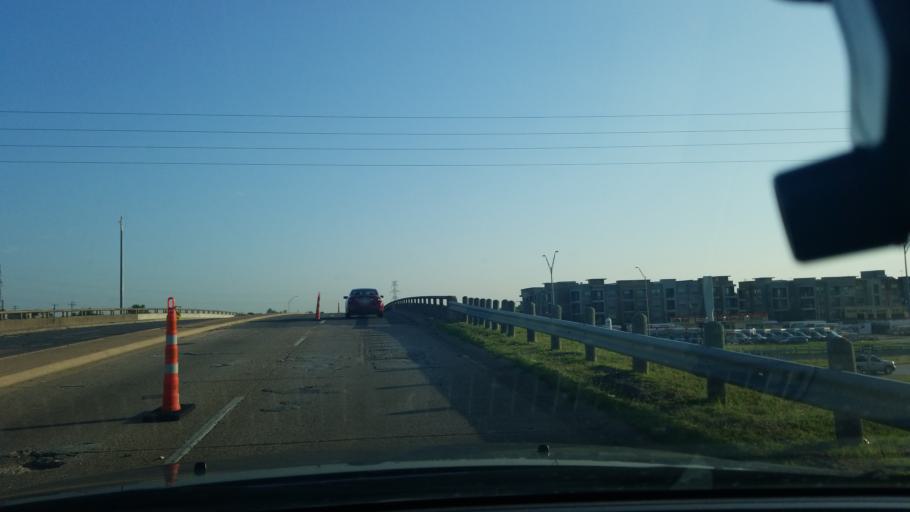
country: US
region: Texas
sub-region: Dallas County
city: Mesquite
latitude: 32.7917
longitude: -96.6338
